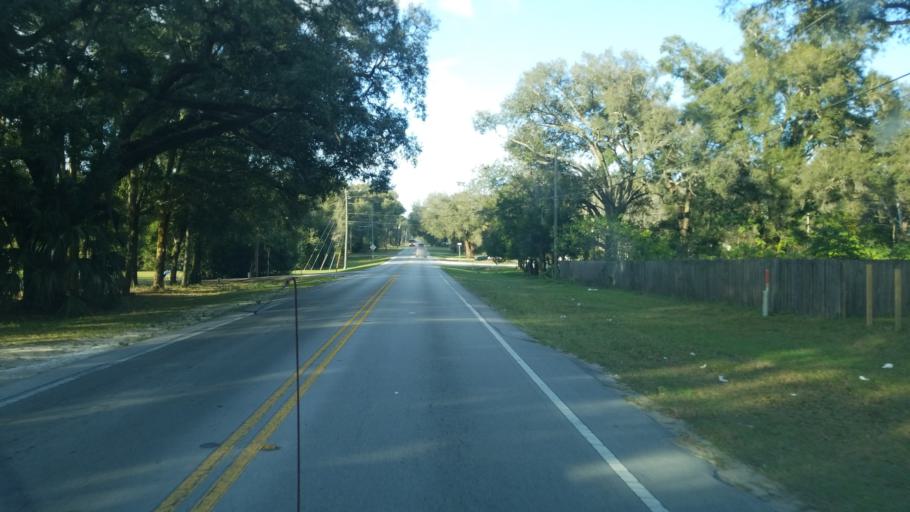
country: US
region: Florida
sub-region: Marion County
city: Ocala
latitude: 29.2684
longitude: -82.1117
